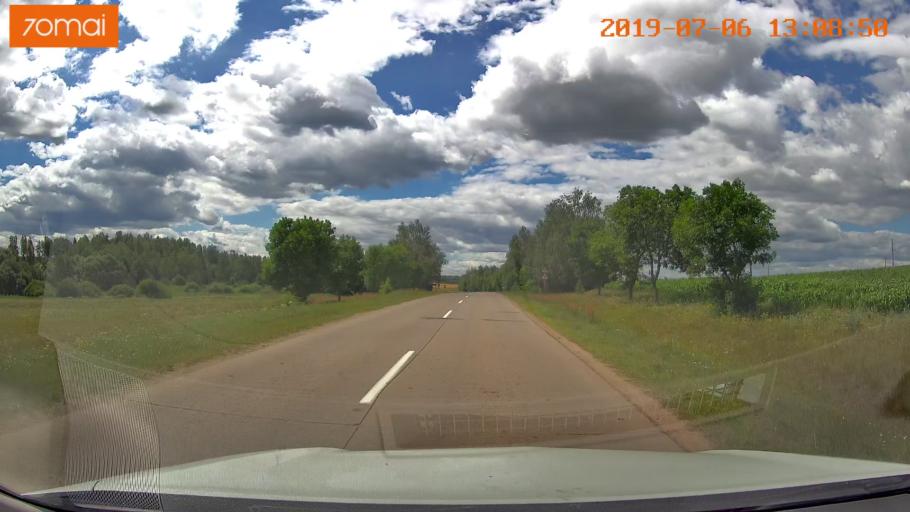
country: BY
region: Minsk
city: Enyerhyetykaw
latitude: 53.6661
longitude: 27.0175
